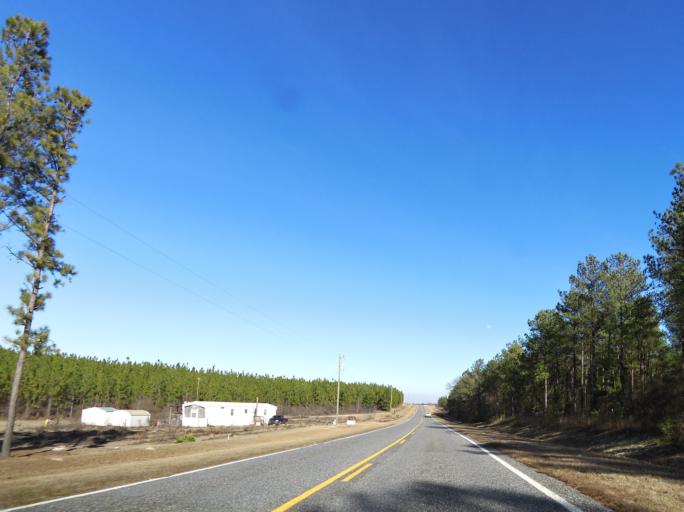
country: US
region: Georgia
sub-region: Crawford County
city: Knoxville
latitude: 32.7333
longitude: -83.9326
